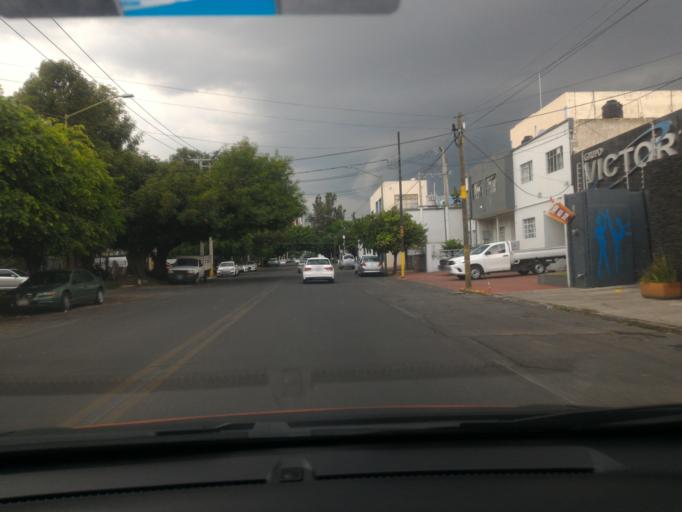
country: MX
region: Jalisco
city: Guadalajara
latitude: 20.6650
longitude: -103.3614
